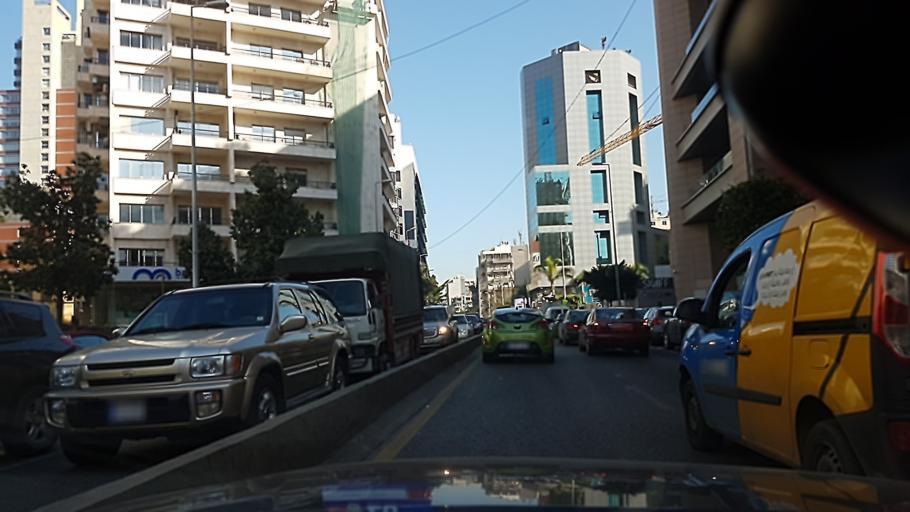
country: LB
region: Beyrouth
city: Beirut
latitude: 33.8922
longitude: 35.5138
